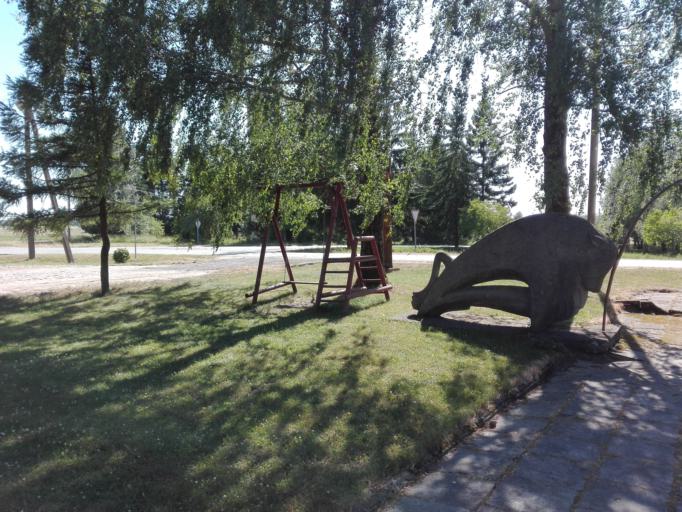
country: LT
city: Vabalninkas
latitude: 56.0269
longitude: 24.6599
